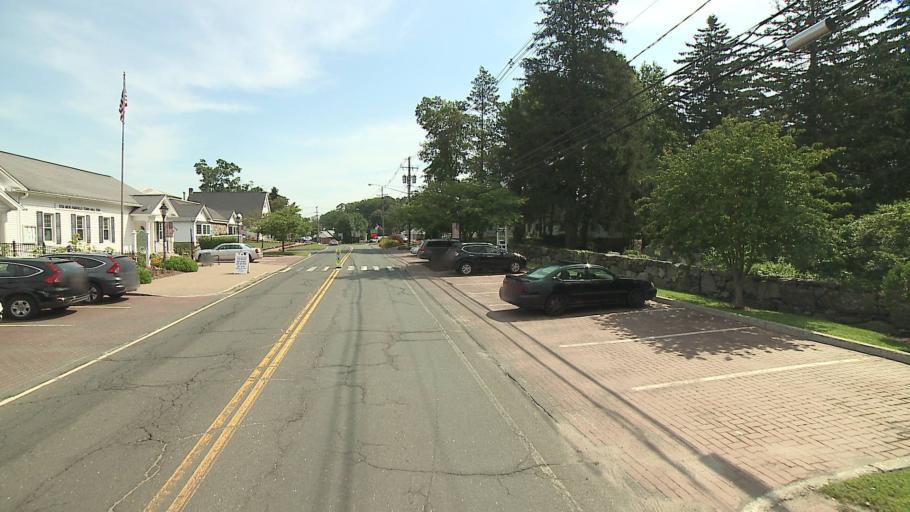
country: US
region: New York
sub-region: Putnam County
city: Putnam Lake
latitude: 41.4653
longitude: -73.4871
